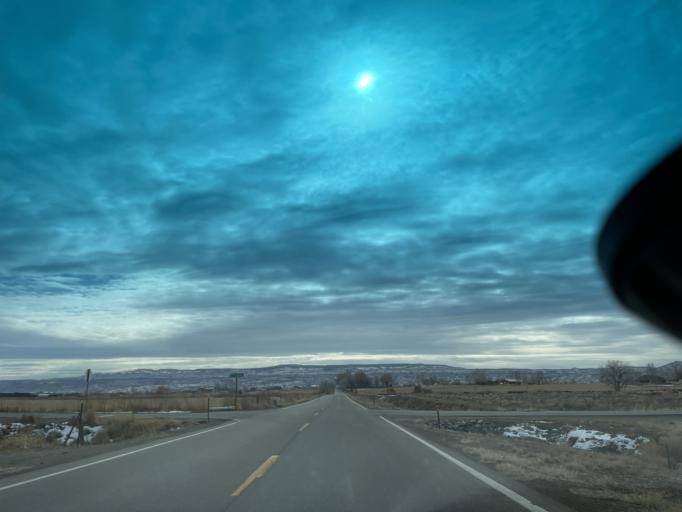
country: US
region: Colorado
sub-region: Mesa County
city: Loma
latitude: 39.2300
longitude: -108.8130
